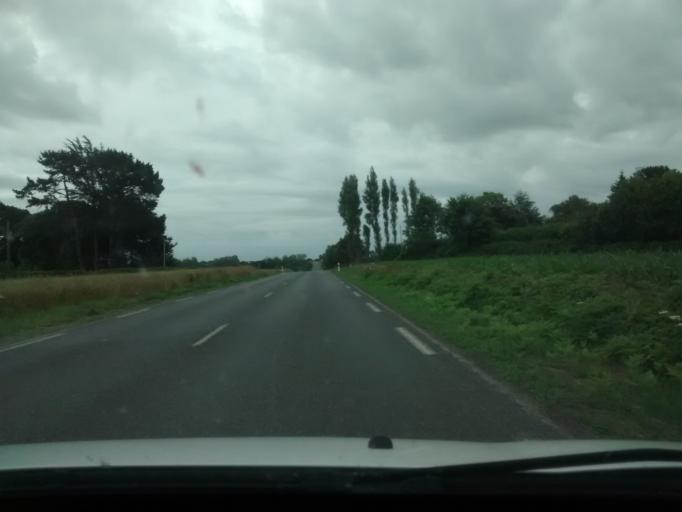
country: FR
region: Brittany
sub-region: Departement des Cotes-d'Armor
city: Louannec
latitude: 48.7797
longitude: -3.3840
